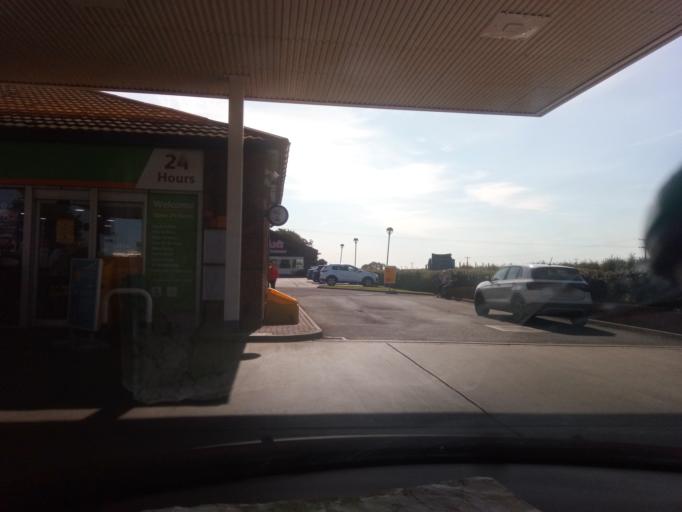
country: GB
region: England
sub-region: Stockton-on-Tees
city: Yarm
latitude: 54.4159
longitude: -1.3192
